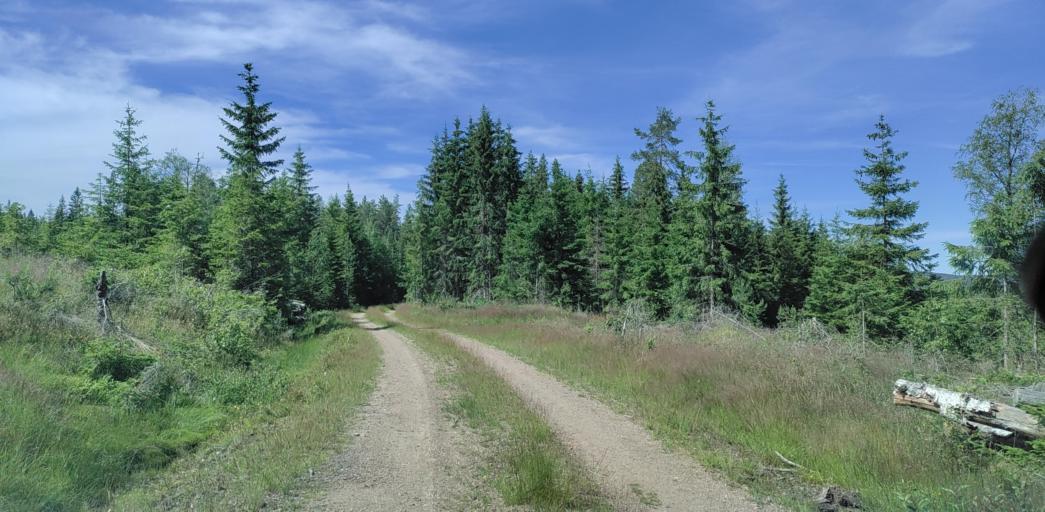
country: SE
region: Vaermland
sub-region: Hagfors Kommun
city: Ekshaerad
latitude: 60.0929
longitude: 13.3755
